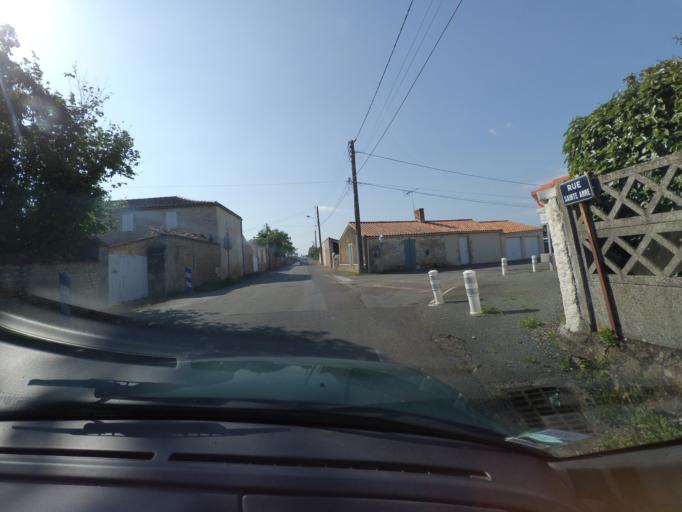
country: FR
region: Pays de la Loire
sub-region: Departement de la Vendee
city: Angles
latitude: 46.4074
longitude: -1.3827
